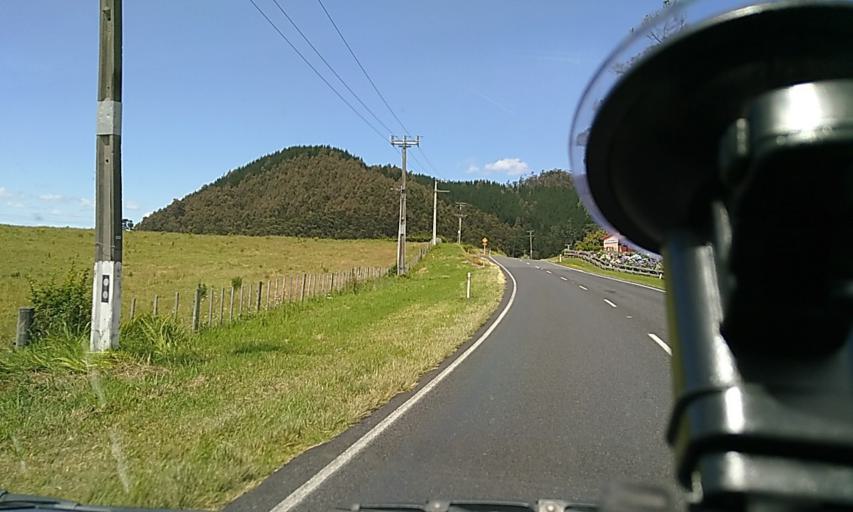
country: NZ
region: Bay of Plenty
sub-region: Western Bay of Plenty District
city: Waihi Beach
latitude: -37.4571
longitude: 175.9327
